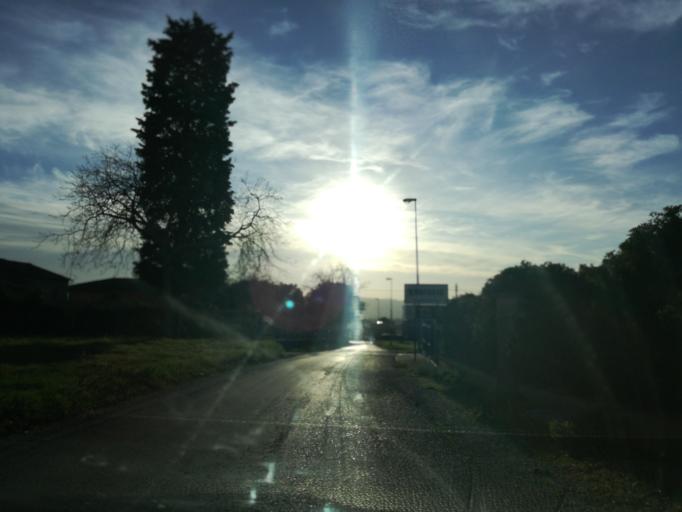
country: IT
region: Umbria
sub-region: Provincia di Perugia
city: Rivotorto
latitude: 43.0471
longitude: 12.6219
